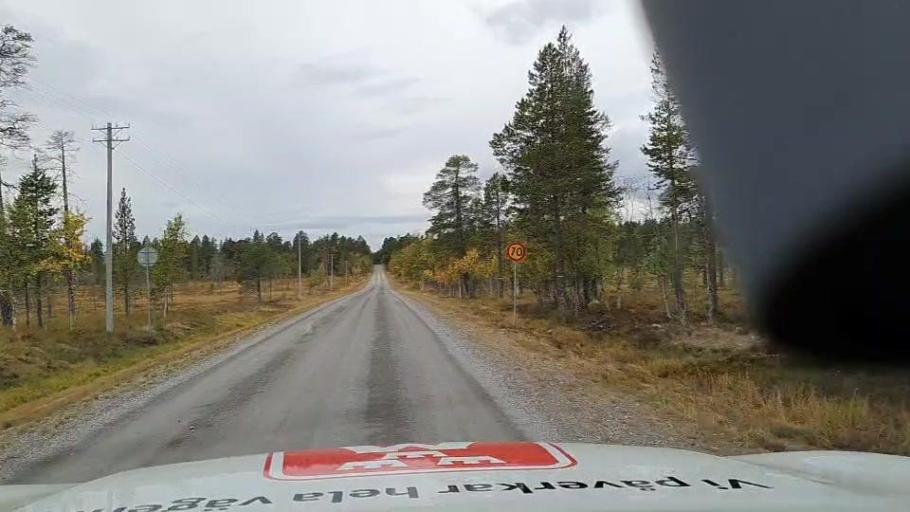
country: NO
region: Hedmark
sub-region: Engerdal
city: Engerdal
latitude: 62.0928
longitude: 12.7934
